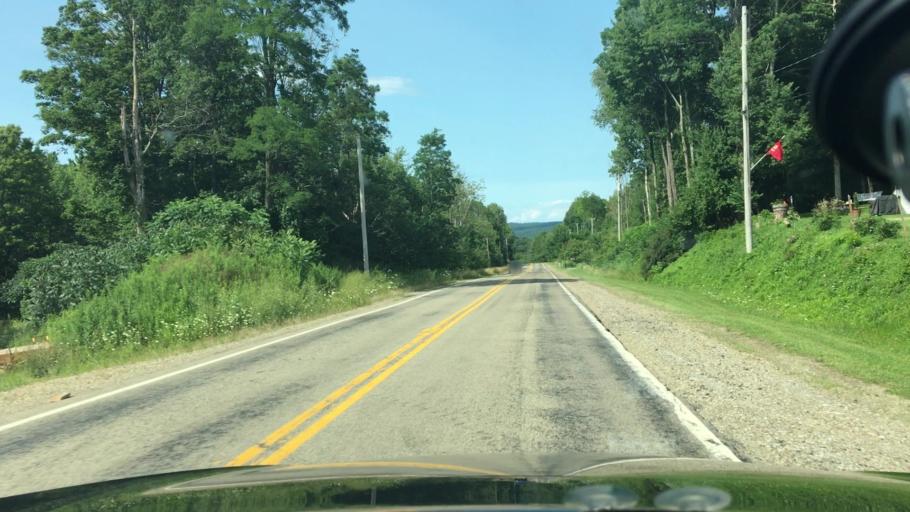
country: US
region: New York
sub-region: Chautauqua County
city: Lakewood
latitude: 42.2453
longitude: -79.3576
